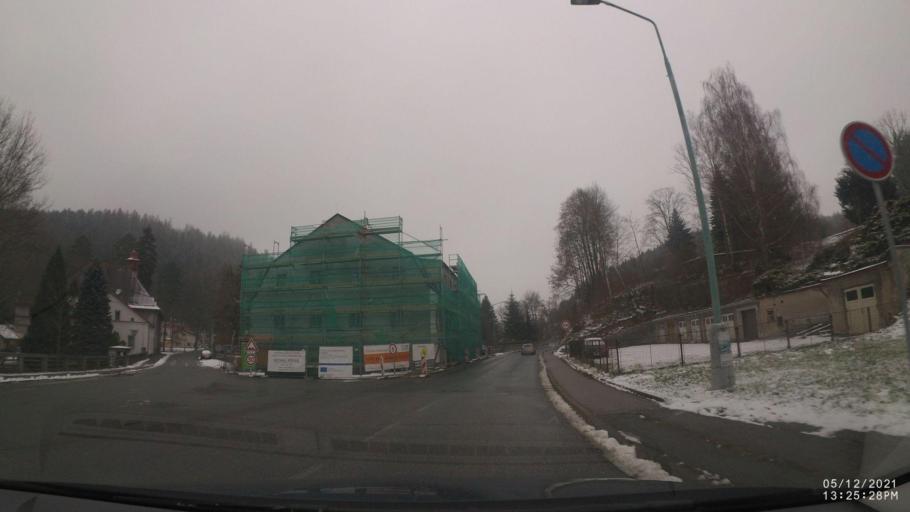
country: CZ
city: Hronov
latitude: 50.4828
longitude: 16.1813
